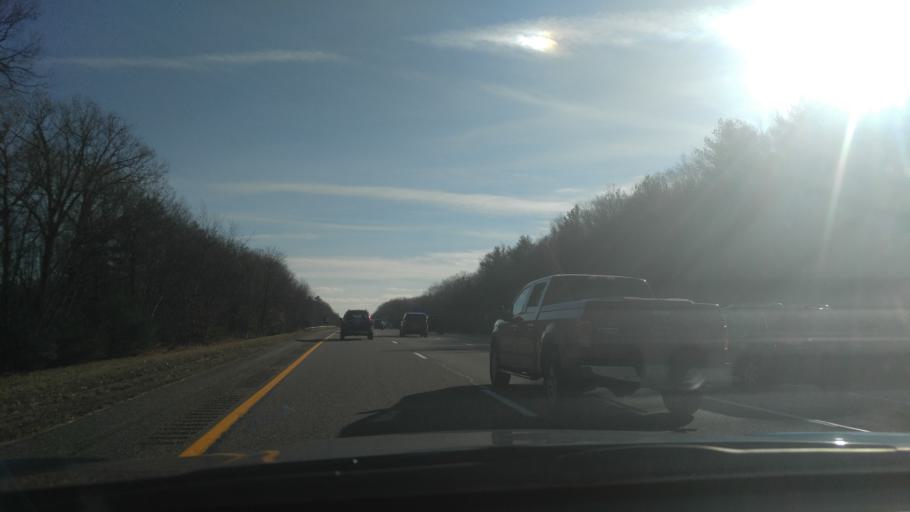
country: US
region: Rhode Island
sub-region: Providence County
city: Greenville
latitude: 41.8906
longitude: -71.5222
